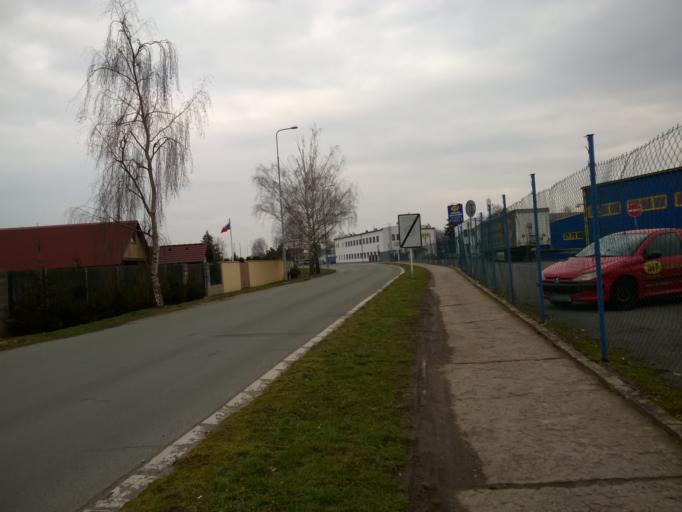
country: CZ
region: Pardubicky
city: Stare Hradiste
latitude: 50.0626
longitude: 15.7643
